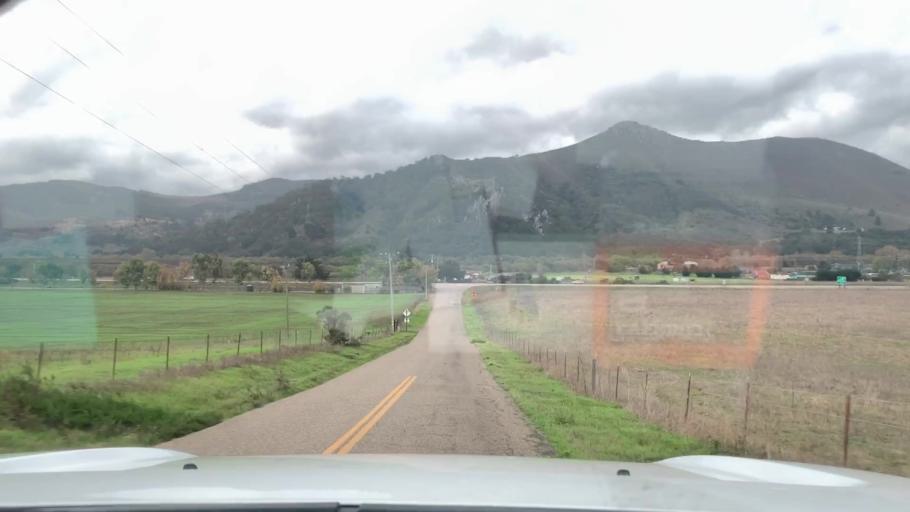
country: US
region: California
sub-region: San Luis Obispo County
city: Morro Bay
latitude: 35.3645
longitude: -120.8066
